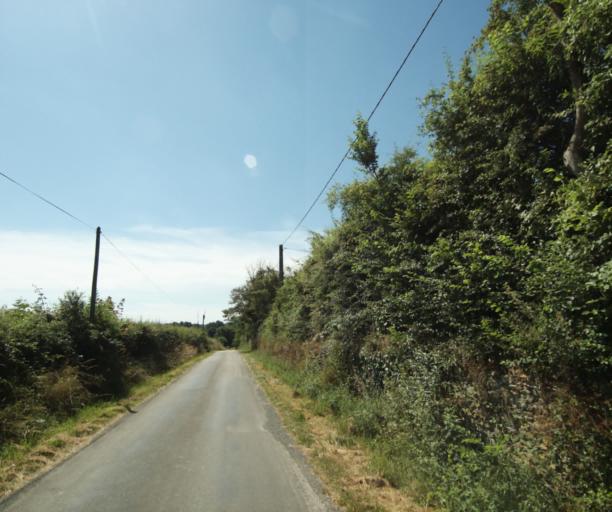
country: FR
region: Pays de la Loire
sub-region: Departement de la Mayenne
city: Laval
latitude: 48.0699
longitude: -0.7454
